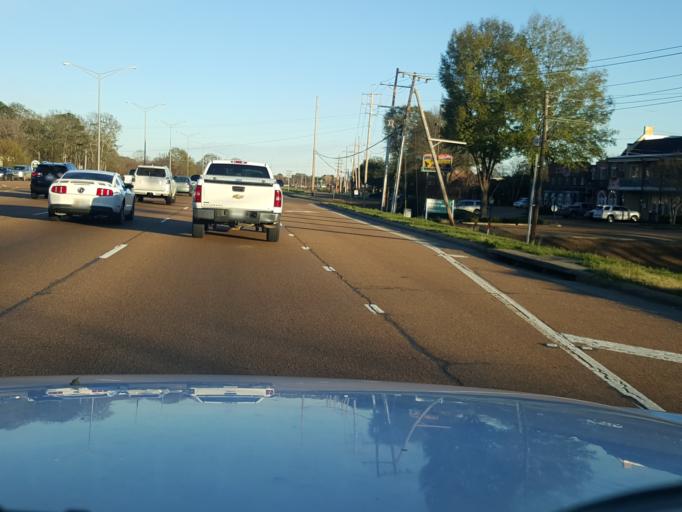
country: US
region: Mississippi
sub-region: Rankin County
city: Flowood
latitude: 32.3339
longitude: -90.1413
